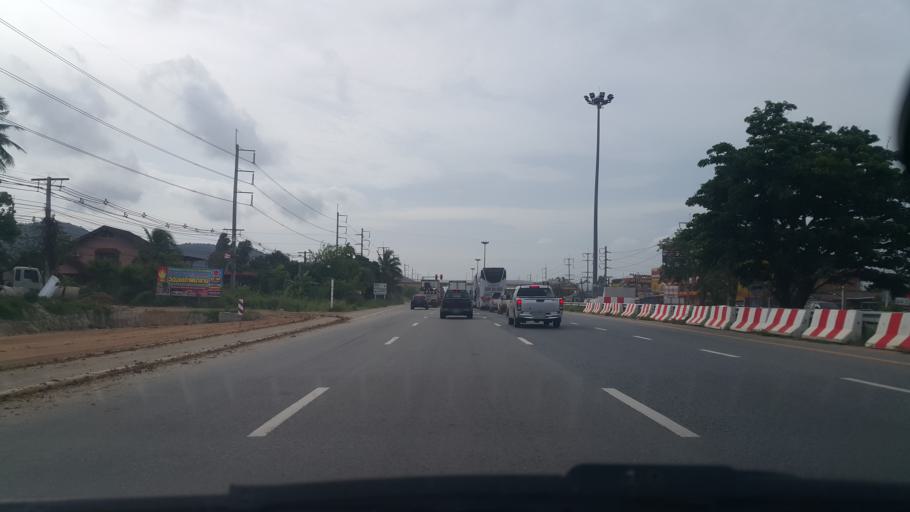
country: TH
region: Rayong
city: Nikhom Phattana
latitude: 12.8105
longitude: 101.1414
